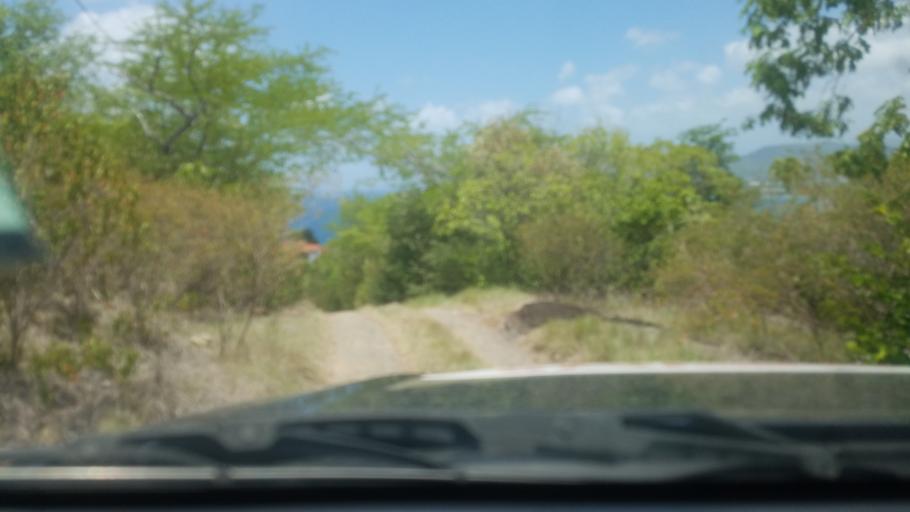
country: LC
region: Vieux-Fort
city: Vieux Fort
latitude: 13.7142
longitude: -60.9504
